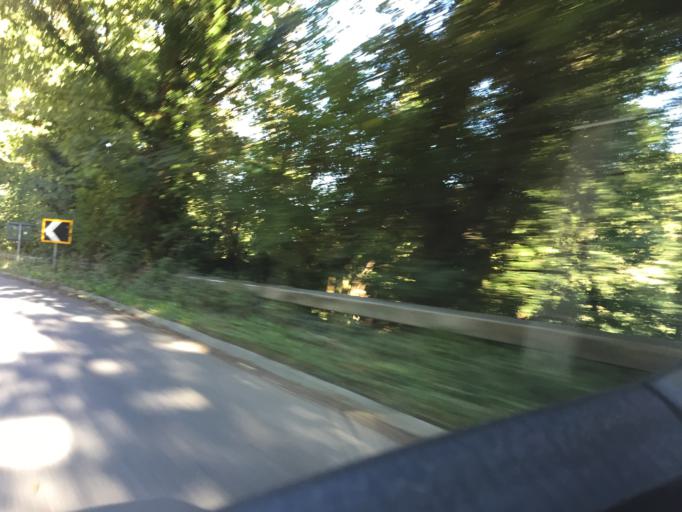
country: GB
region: England
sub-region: Wiltshire
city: Biddestone
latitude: 51.4727
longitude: -2.2201
